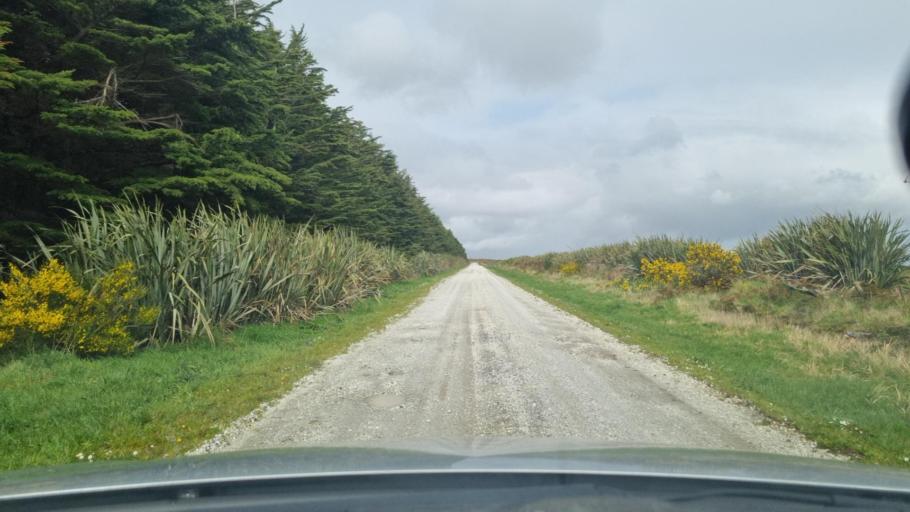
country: NZ
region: Southland
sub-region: Invercargill City
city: Bluff
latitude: -46.5148
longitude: 168.3578
